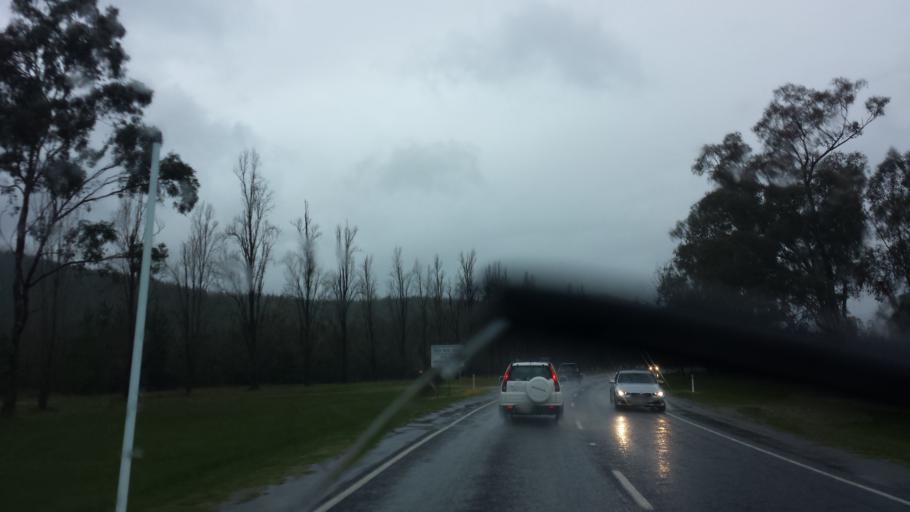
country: AU
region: Victoria
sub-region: Alpine
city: Mount Beauty
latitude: -36.5829
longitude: 146.7546
